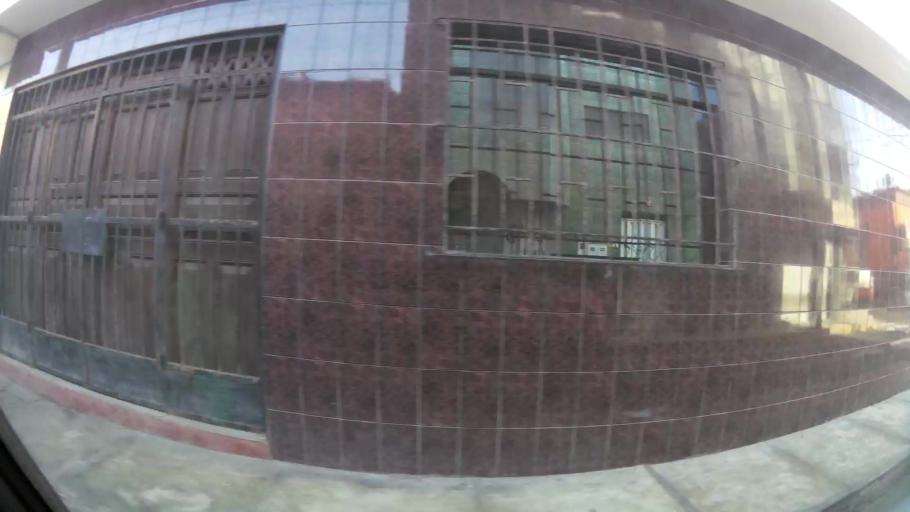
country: PE
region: Lima
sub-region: Huaura
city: Huacho
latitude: -11.1103
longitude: -77.6107
